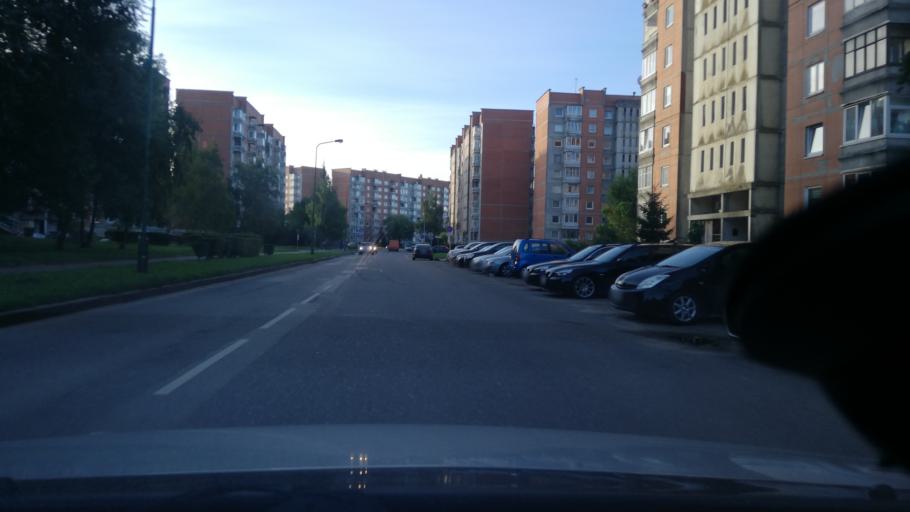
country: LT
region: Klaipedos apskritis
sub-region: Klaipeda
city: Klaipeda
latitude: 55.6691
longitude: 21.2004
